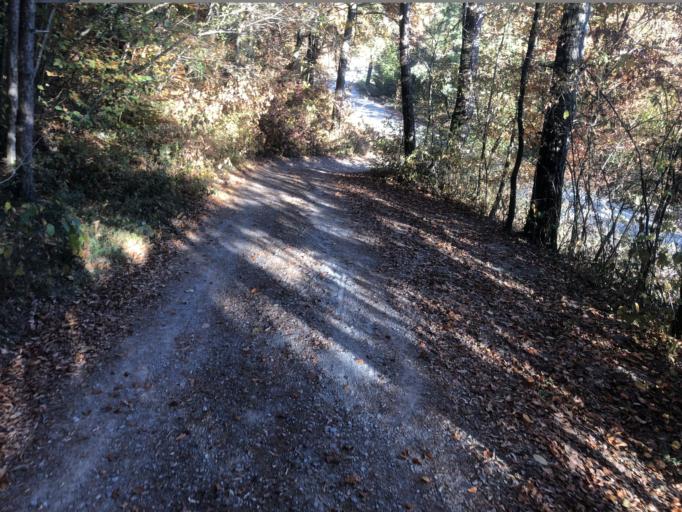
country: DE
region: Baden-Wuerttemberg
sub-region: Regierungsbezirk Stuttgart
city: Hildrizhausen
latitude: 48.5739
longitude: 8.9759
